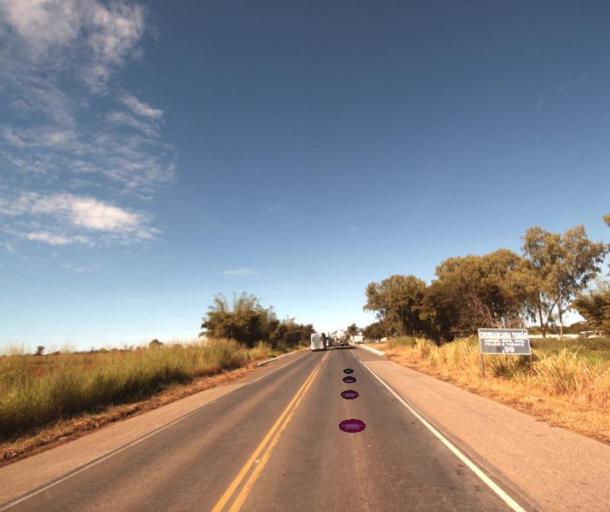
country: BR
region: Goias
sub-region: Itapaci
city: Itapaci
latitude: -14.8534
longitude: -49.3186
